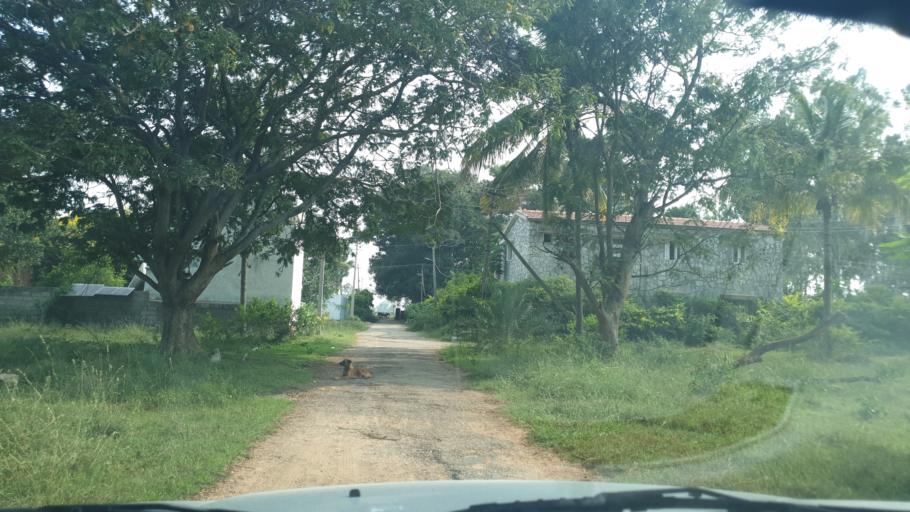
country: IN
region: Karnataka
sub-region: Bangalore Urban
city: Yelahanka
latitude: 13.0704
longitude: 77.6691
